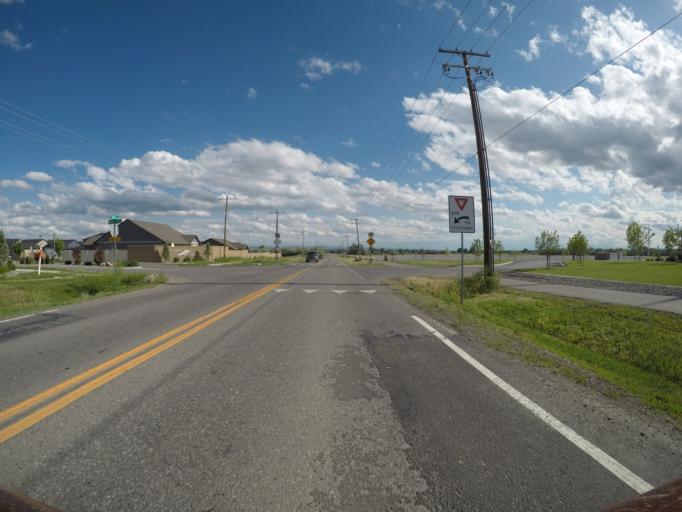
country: US
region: Montana
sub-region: Yellowstone County
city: Billings
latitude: 45.7967
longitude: -108.6527
